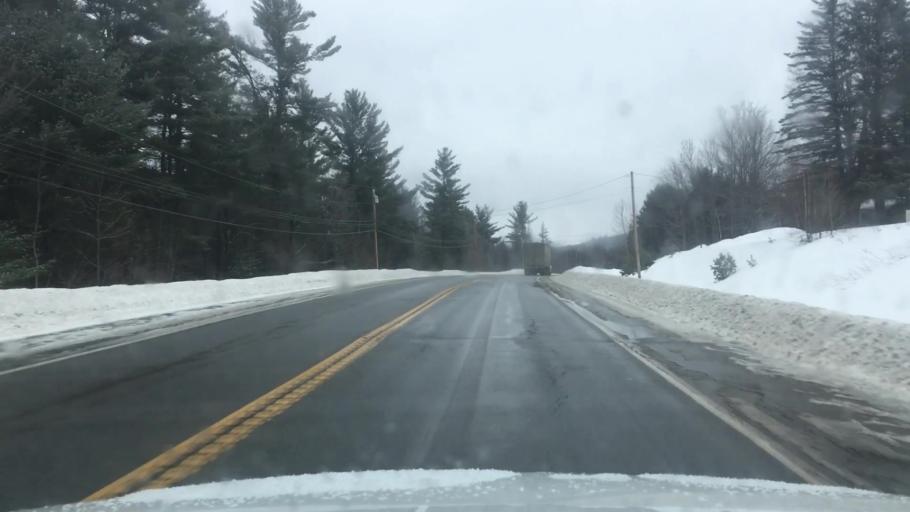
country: US
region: Maine
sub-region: Oxford County
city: Peru
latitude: 44.5572
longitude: -70.3786
